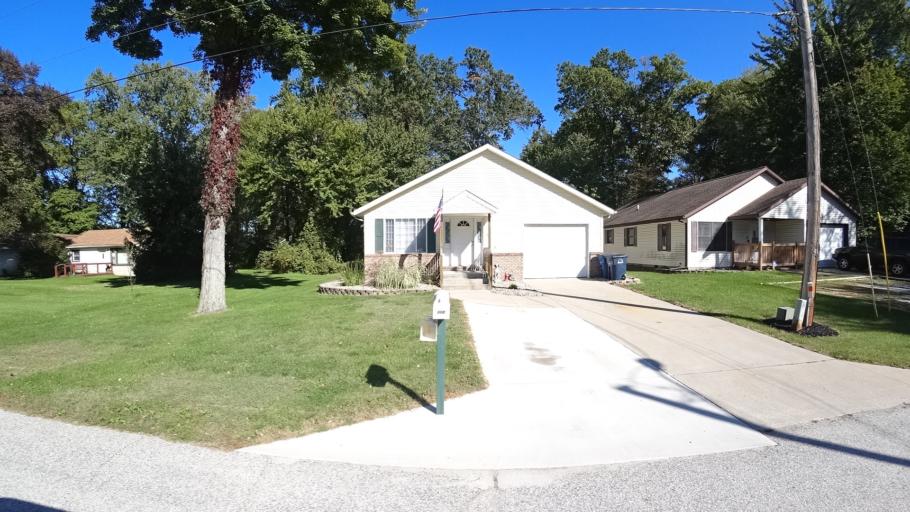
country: US
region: Indiana
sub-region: LaPorte County
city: Long Beach
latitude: 41.7434
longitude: -86.8292
